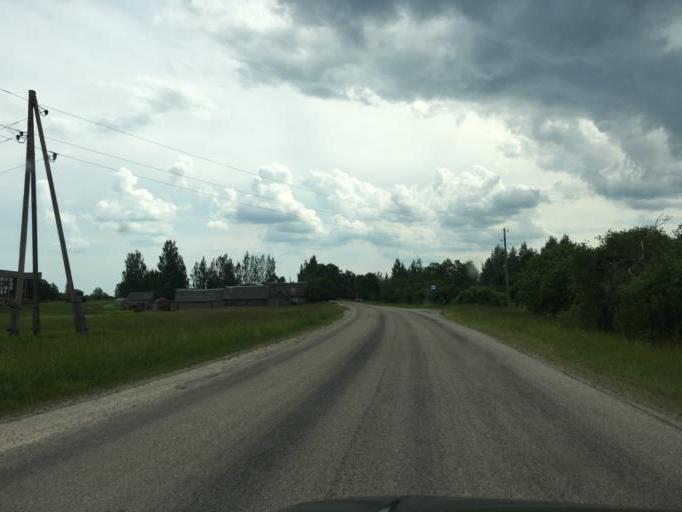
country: LV
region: Rugaju
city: Rugaji
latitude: 56.9086
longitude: 27.0650
